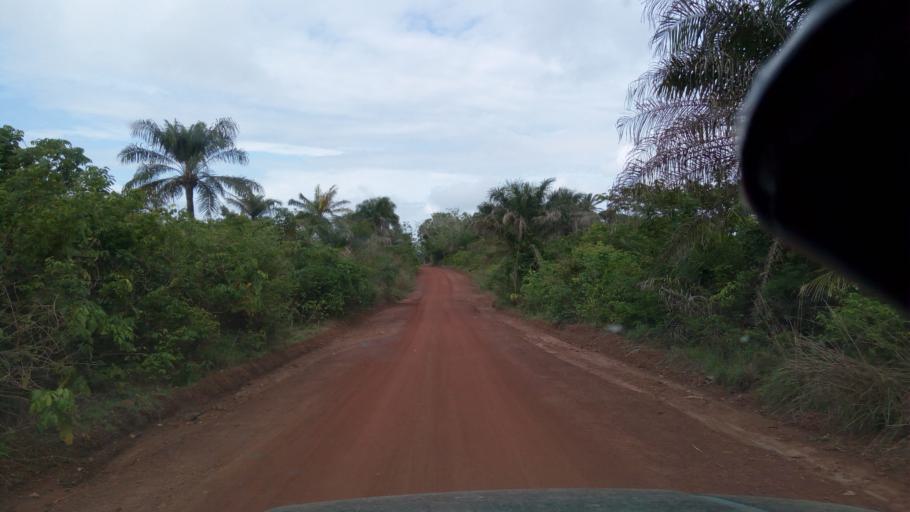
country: SL
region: Northern Province
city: Pepel
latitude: 8.6182
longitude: -13.0441
